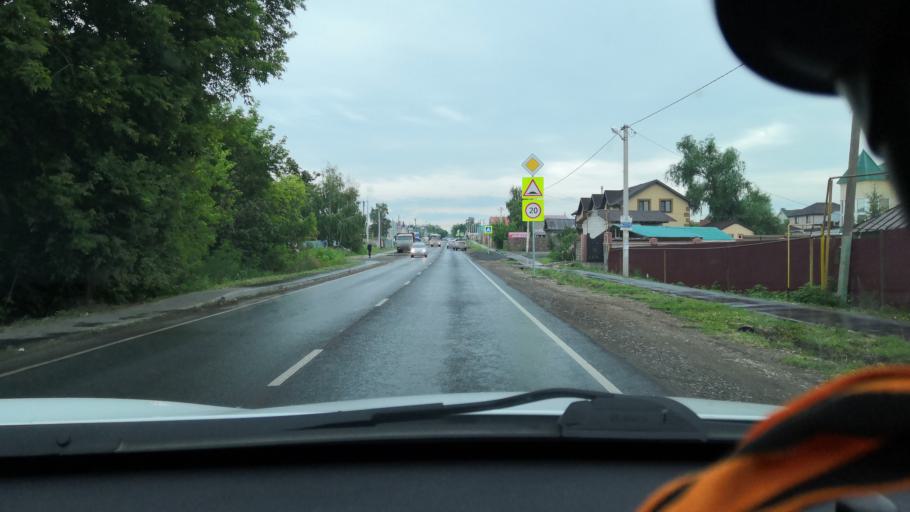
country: RU
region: Samara
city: Novosemeykino
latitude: 53.3778
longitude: 50.3445
